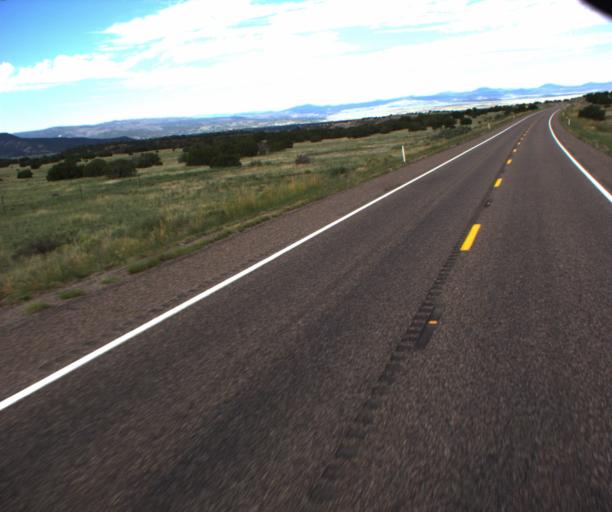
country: US
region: Arizona
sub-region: Apache County
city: Springerville
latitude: 34.1458
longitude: -109.2112
